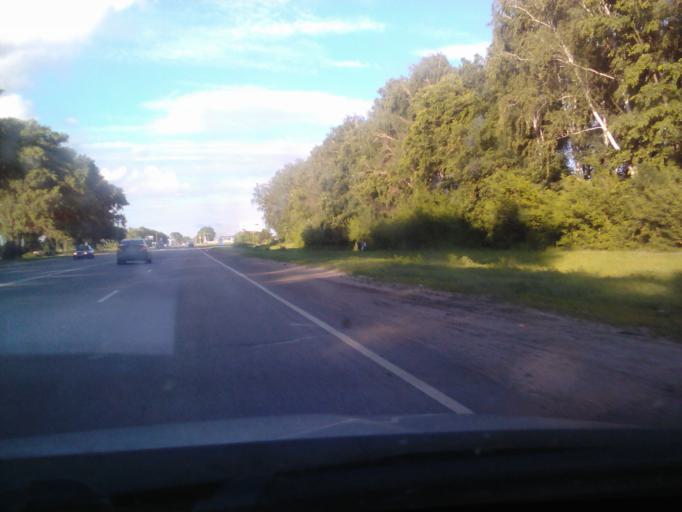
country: RU
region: Kursk
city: Kurchatov
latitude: 51.6575
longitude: 35.7065
